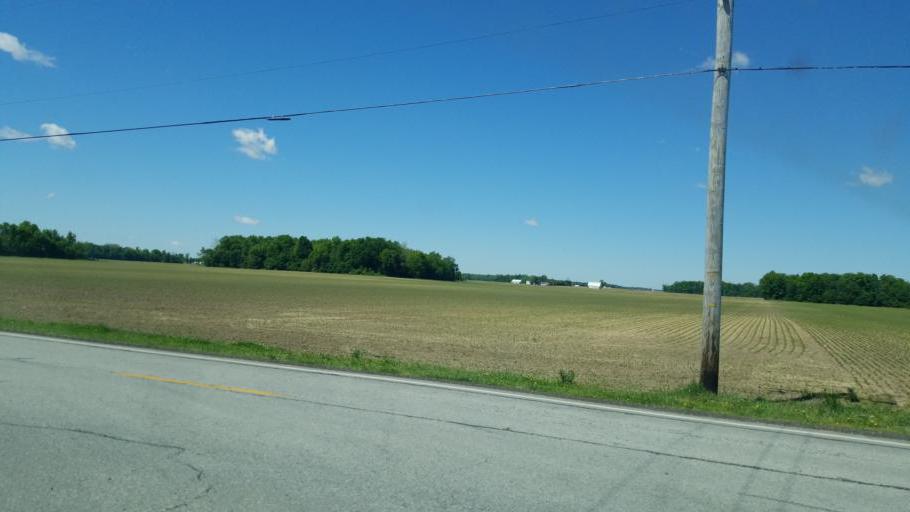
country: US
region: Ohio
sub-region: Shelby County
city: Jackson Center
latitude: 40.4180
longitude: -84.0405
